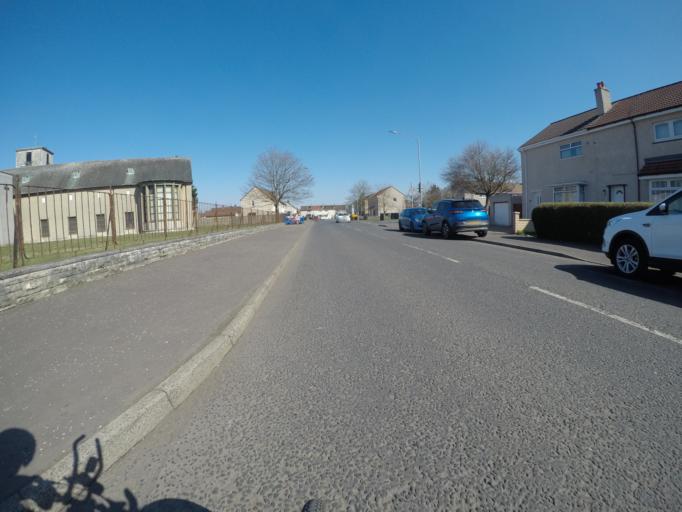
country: GB
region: Scotland
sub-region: North Ayrshire
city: Irvine
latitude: 55.6237
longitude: -4.6605
